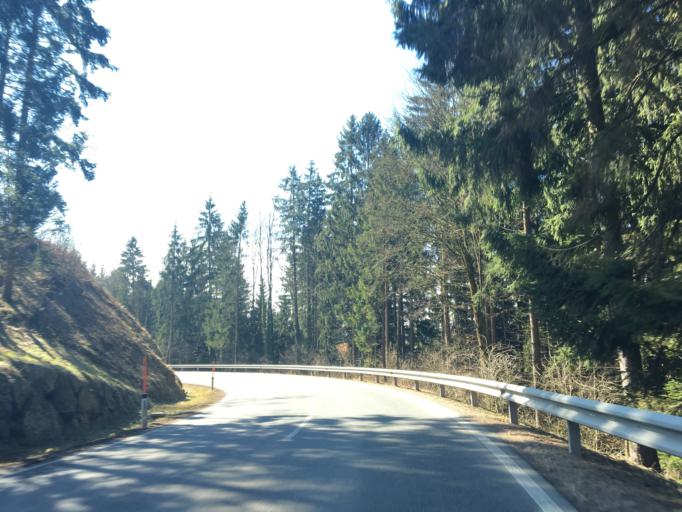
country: AT
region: Upper Austria
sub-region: Politischer Bezirk Perg
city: Sankt Georgen am Walde
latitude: 48.2942
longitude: 14.8990
